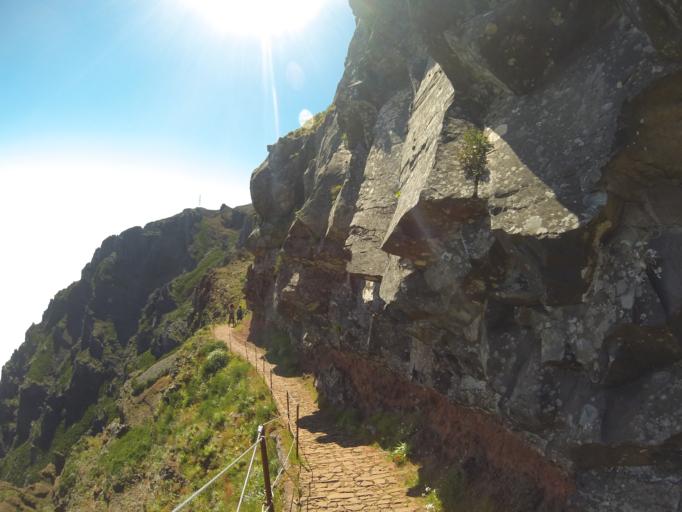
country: PT
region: Madeira
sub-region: Camara de Lobos
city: Curral das Freiras
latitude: 32.7380
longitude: -16.9331
